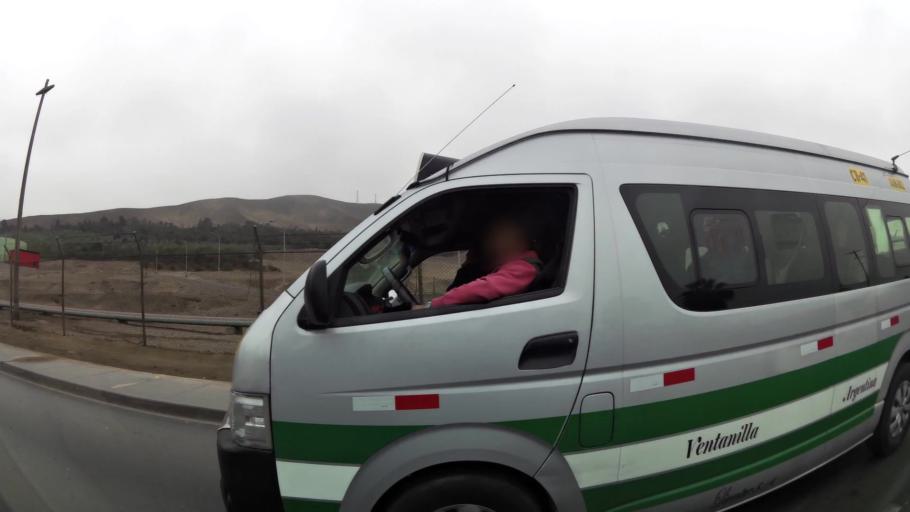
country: PE
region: Lima
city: Ventanilla
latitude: -11.9222
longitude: -77.1290
